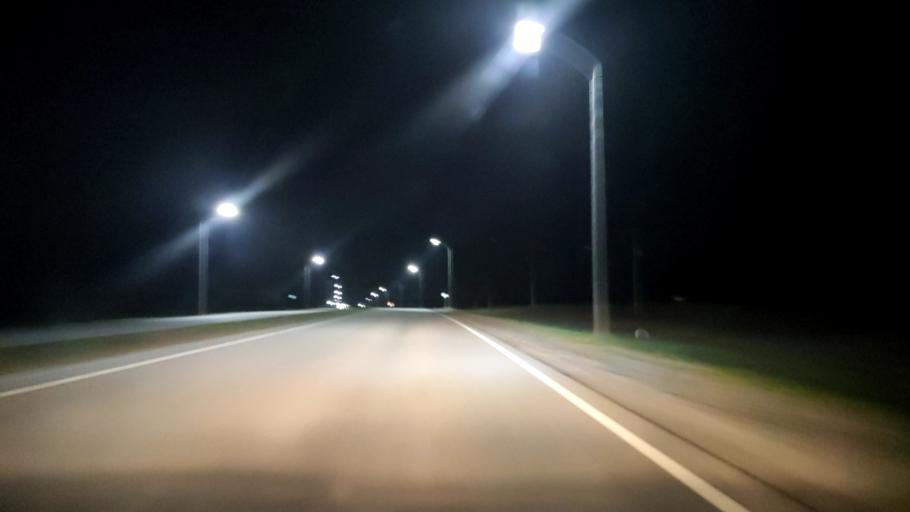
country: RU
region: Belgorod
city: Staryy Oskol
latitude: 51.3946
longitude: 37.8706
